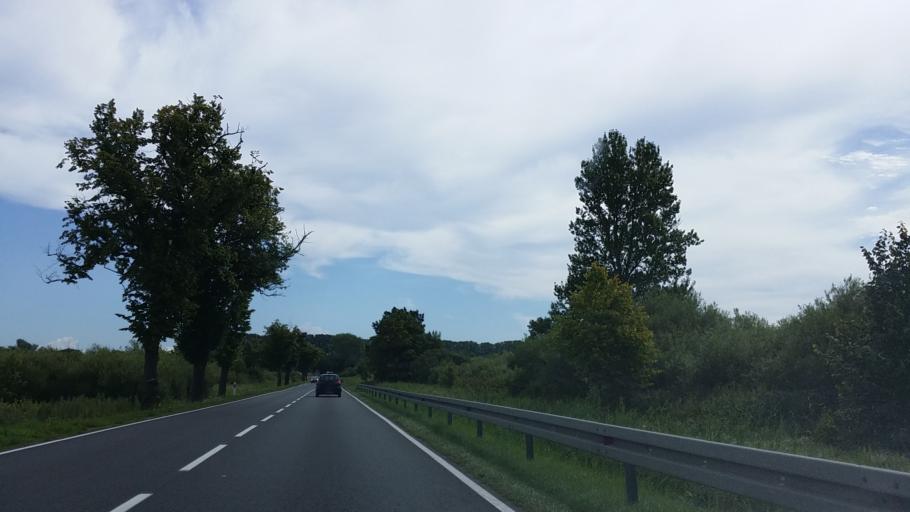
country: PL
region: West Pomeranian Voivodeship
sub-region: Powiat kolobrzeski
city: Kolobrzeg
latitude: 54.1781
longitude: 15.6188
